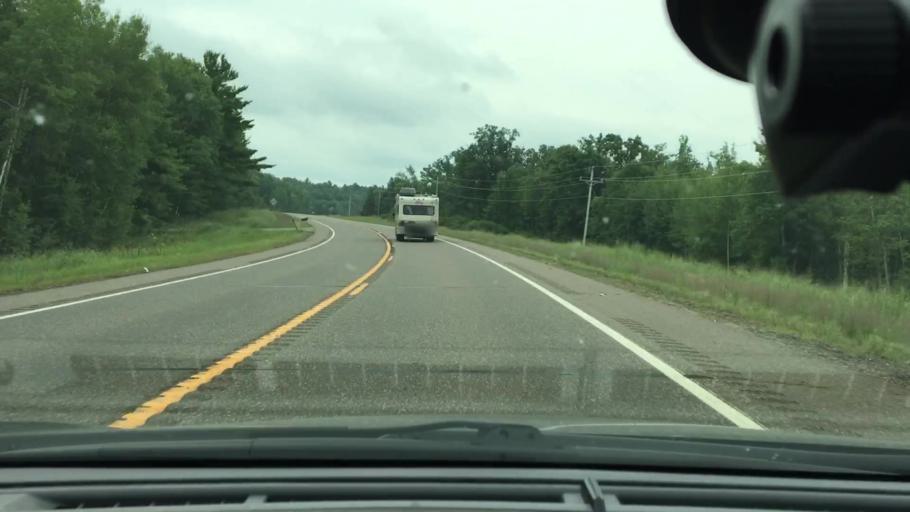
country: US
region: Minnesota
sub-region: Crow Wing County
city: Crosby
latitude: 46.5079
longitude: -93.9599
